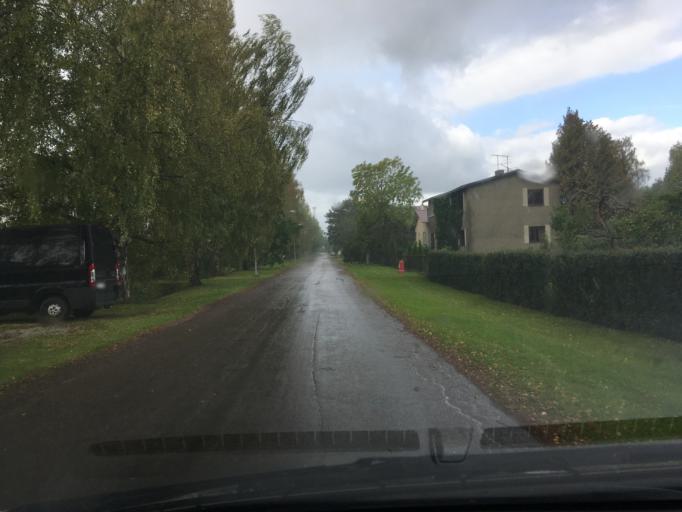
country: EE
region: Raplamaa
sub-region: Rapla vald
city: Rapla
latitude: 58.9922
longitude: 24.8231
